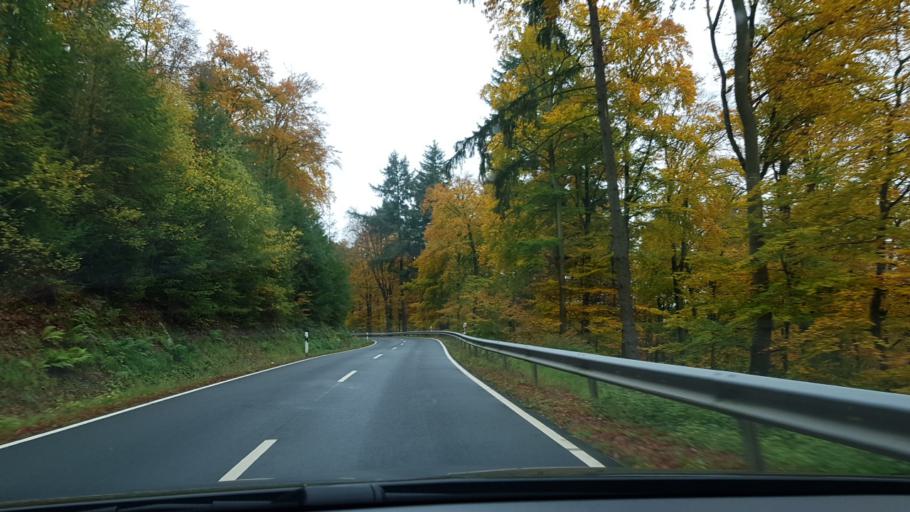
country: DE
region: Rheinland-Pfalz
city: Polich
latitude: 49.7827
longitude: 6.8505
